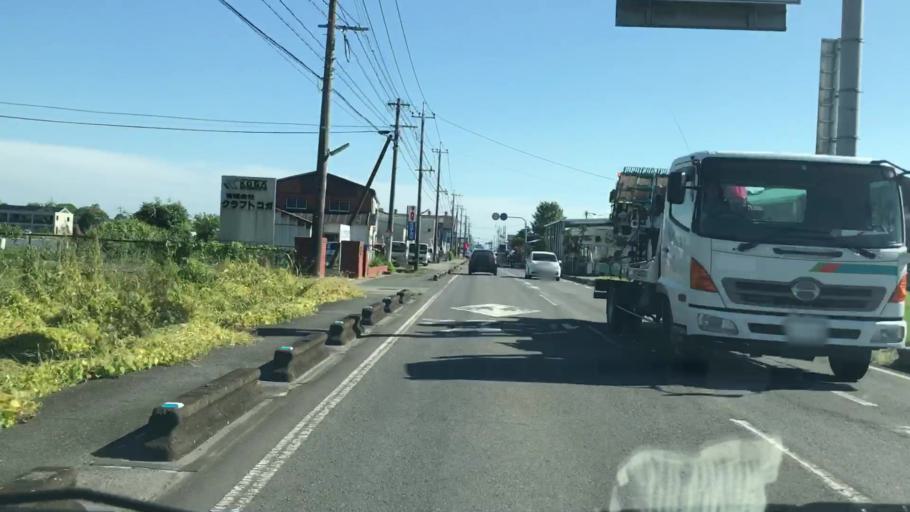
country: JP
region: Saga Prefecture
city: Okawa
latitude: 33.2116
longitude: 130.3355
